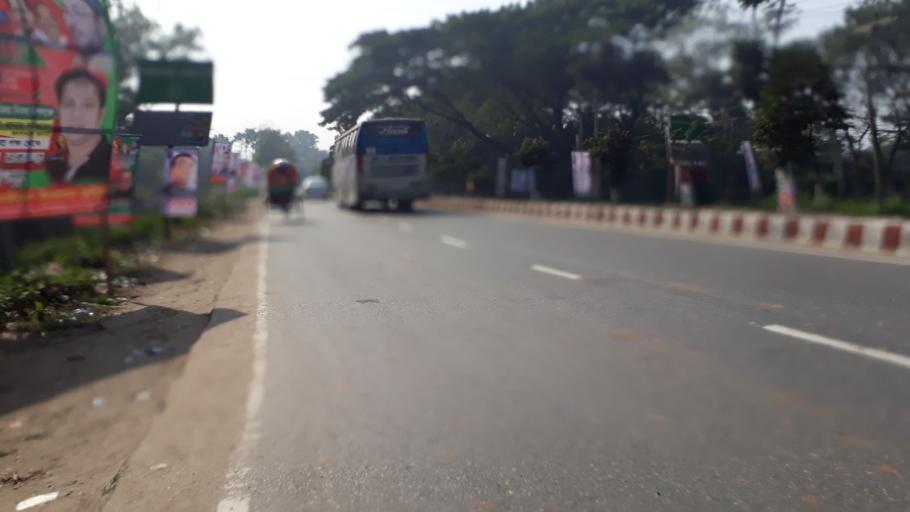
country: BD
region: Dhaka
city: Tungi
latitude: 23.8722
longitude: 90.2732
